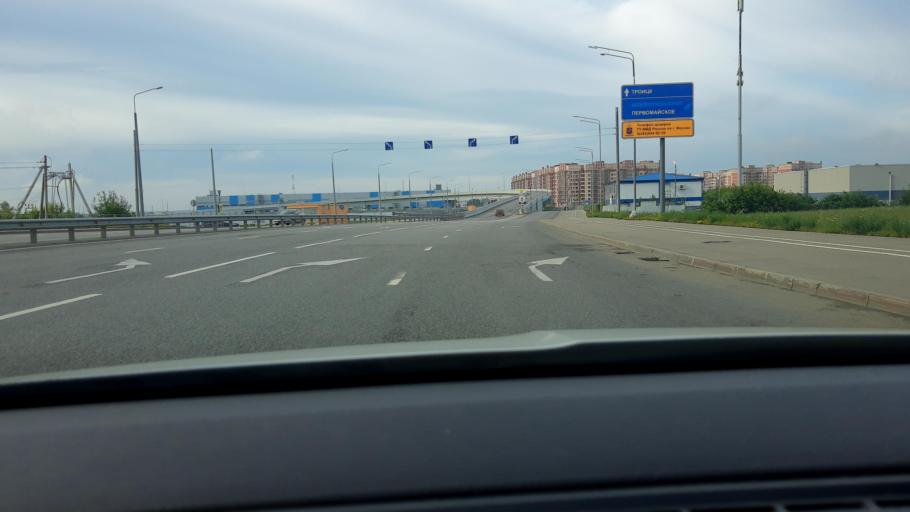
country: RU
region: Moskovskaya
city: Kokoshkino
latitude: 55.5507
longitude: 37.1579
